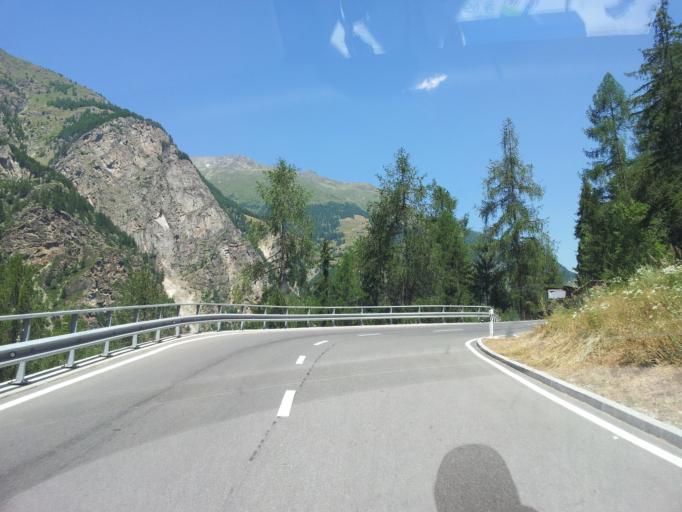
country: CH
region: Valais
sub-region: Visp District
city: Sankt Niklaus
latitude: 46.1874
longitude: 7.8165
